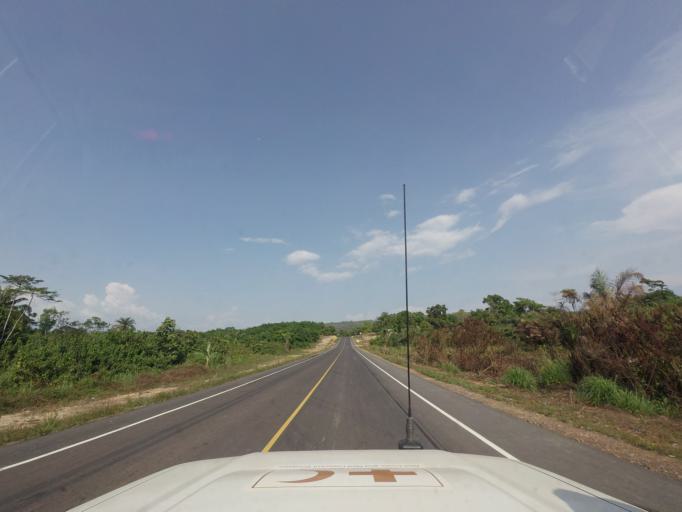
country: LR
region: Margibi
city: Kakata
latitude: 6.7655
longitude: -10.0280
